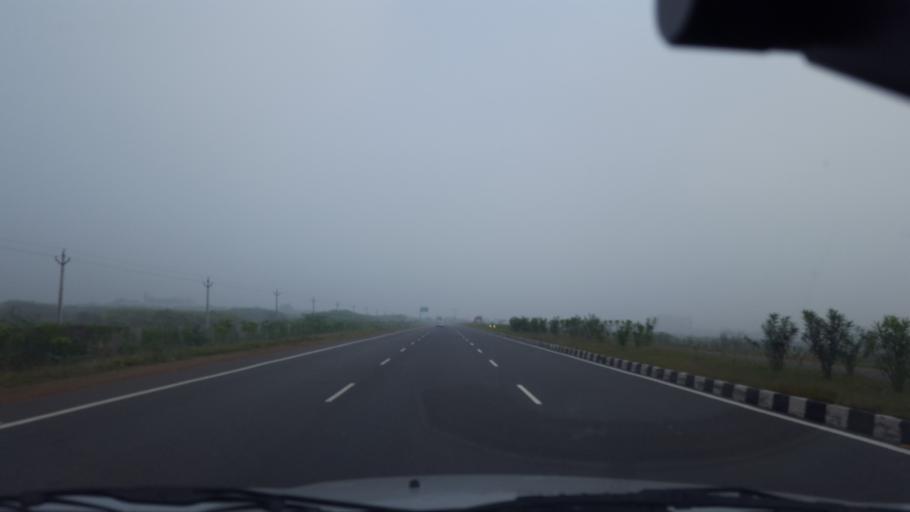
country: IN
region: Andhra Pradesh
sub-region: Prakasam
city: Ongole
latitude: 15.4891
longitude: 80.0647
